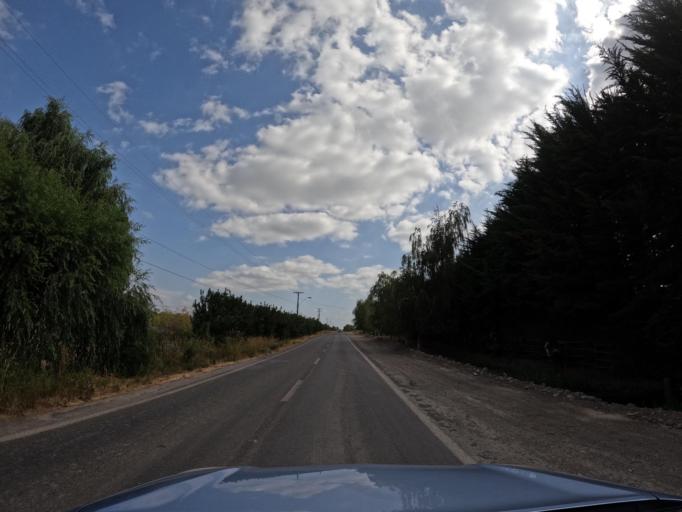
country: CL
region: Maule
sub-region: Provincia de Curico
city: Molina
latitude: -35.1820
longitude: -71.2946
